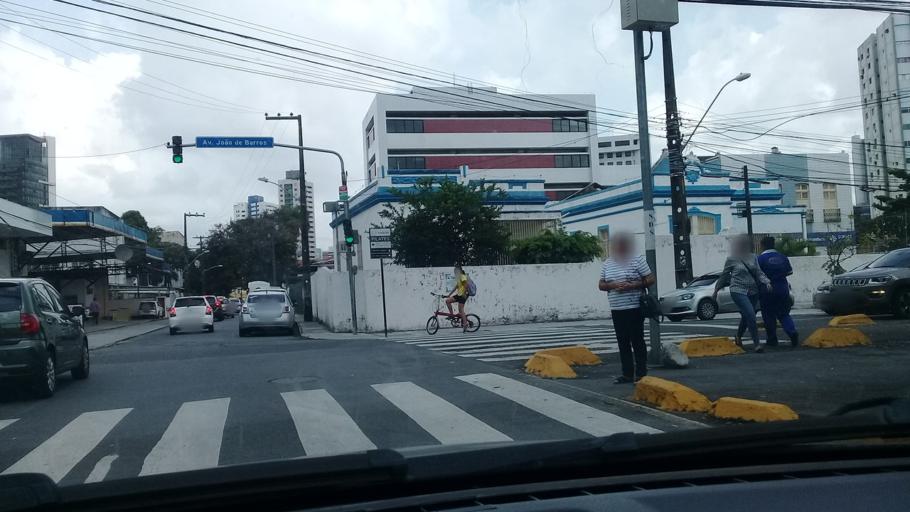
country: BR
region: Pernambuco
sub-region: Recife
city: Recife
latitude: -8.0503
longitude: -34.8897
